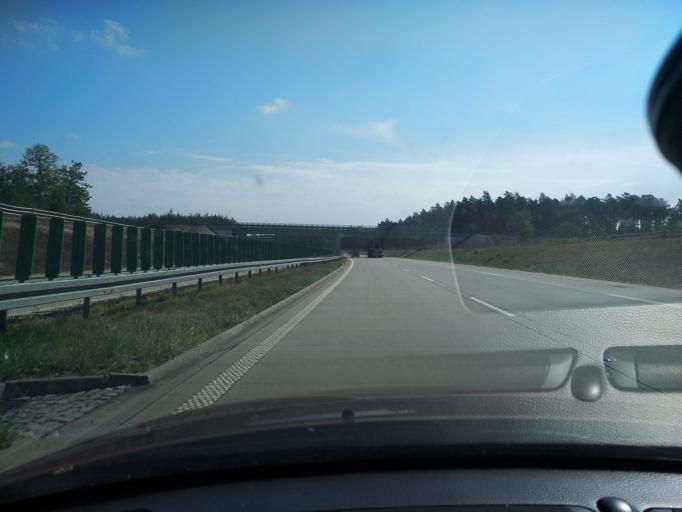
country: PL
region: Lower Silesian Voivodeship
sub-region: Powiat boleslawiecki
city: Nowogrodziec
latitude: 51.2682
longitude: 15.4215
